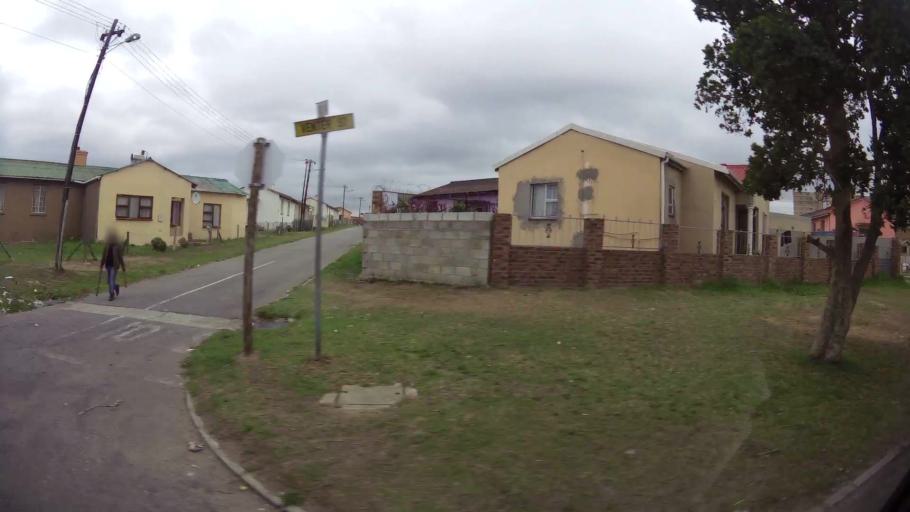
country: ZA
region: Eastern Cape
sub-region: Nelson Mandela Bay Metropolitan Municipality
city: Port Elizabeth
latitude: -33.9049
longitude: 25.5698
